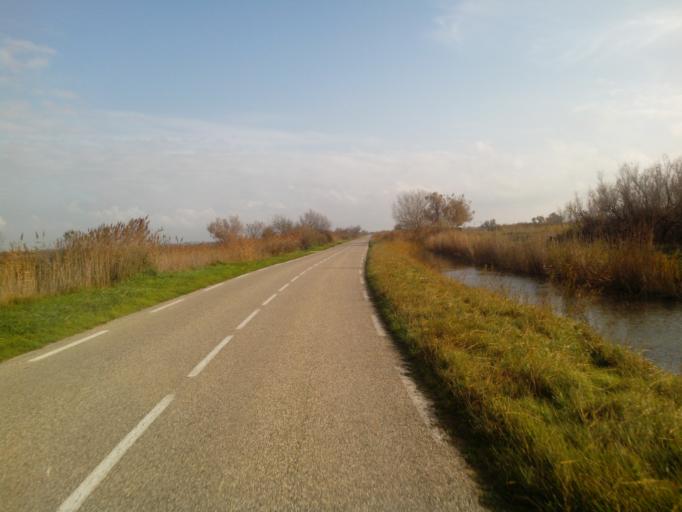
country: FR
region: Languedoc-Roussillon
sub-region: Departement du Gard
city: Saint-Gilles
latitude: 43.5802
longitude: 4.5129
